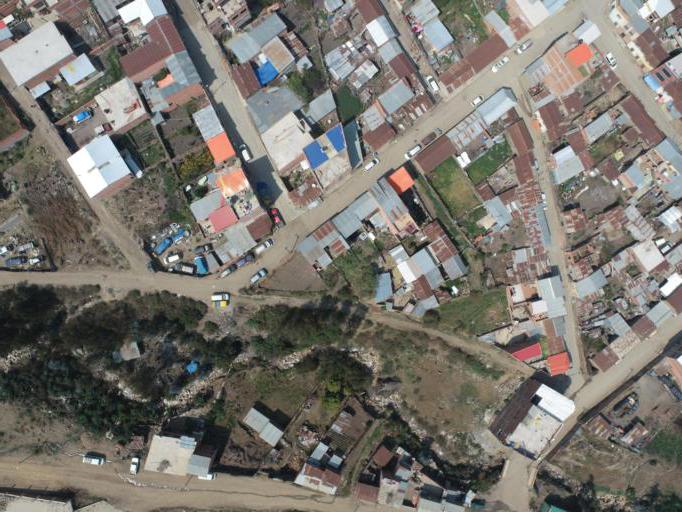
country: BO
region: La Paz
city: Quime
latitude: -16.9830
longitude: -67.2152
